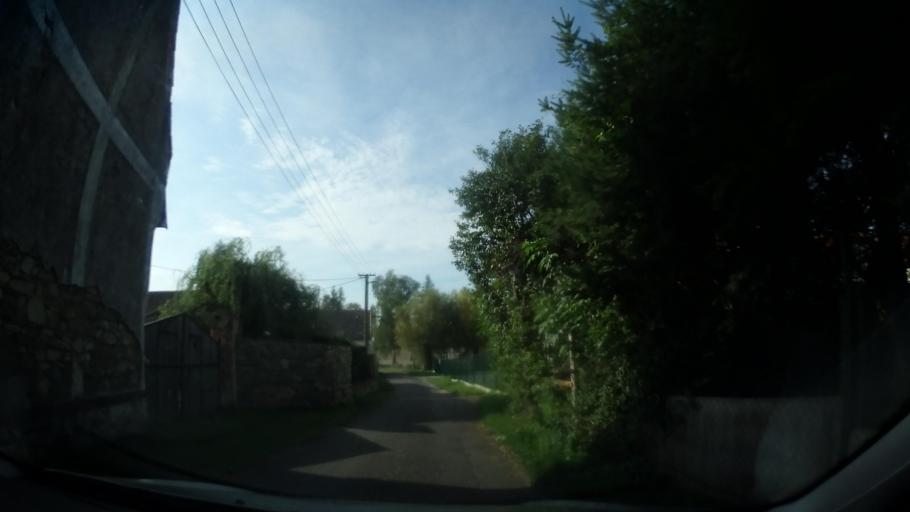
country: CZ
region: Jihocesky
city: Cimelice
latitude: 49.4248
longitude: 14.1213
